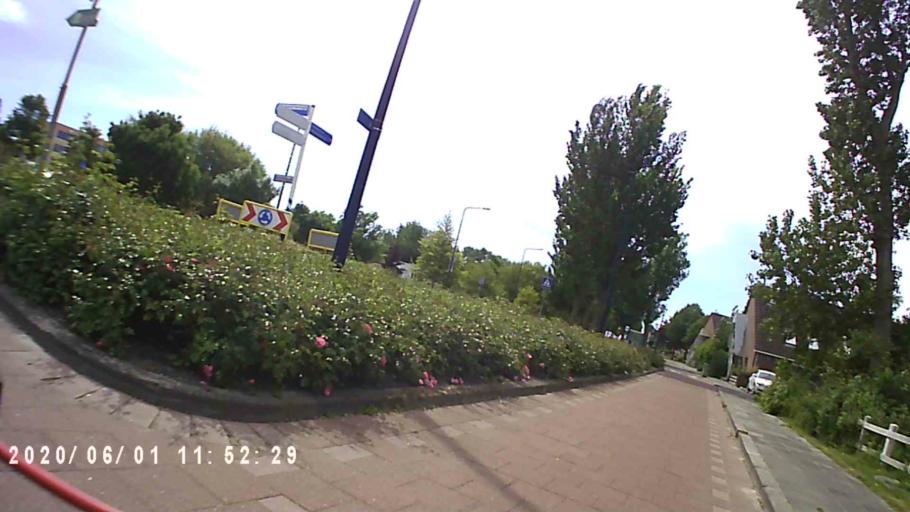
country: NL
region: Friesland
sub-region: Gemeente Harlingen
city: Harlingen
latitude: 53.1633
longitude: 5.4273
